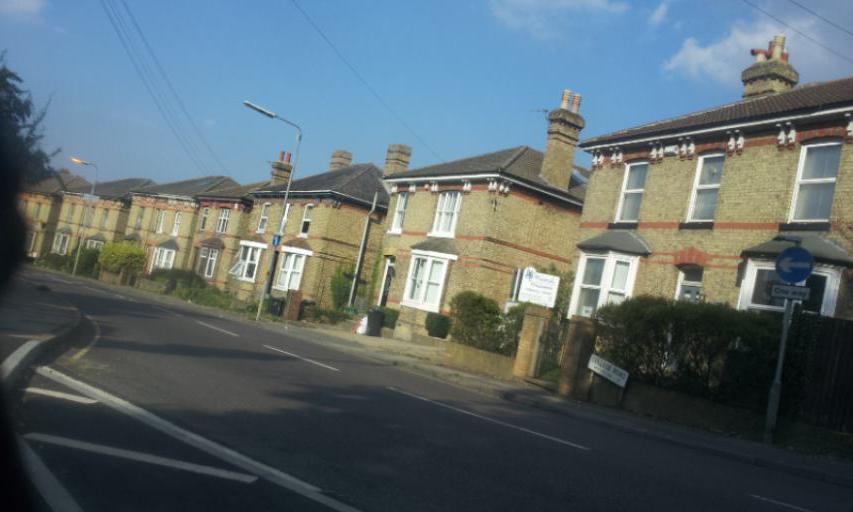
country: GB
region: England
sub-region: Kent
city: Maidstone
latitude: 51.2684
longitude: 0.5227
